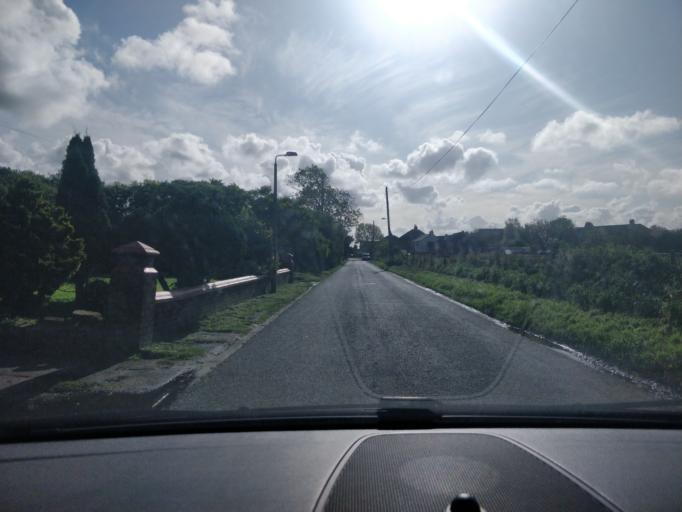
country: GB
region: England
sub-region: Lancashire
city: Banks
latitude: 53.6215
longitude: -2.9388
